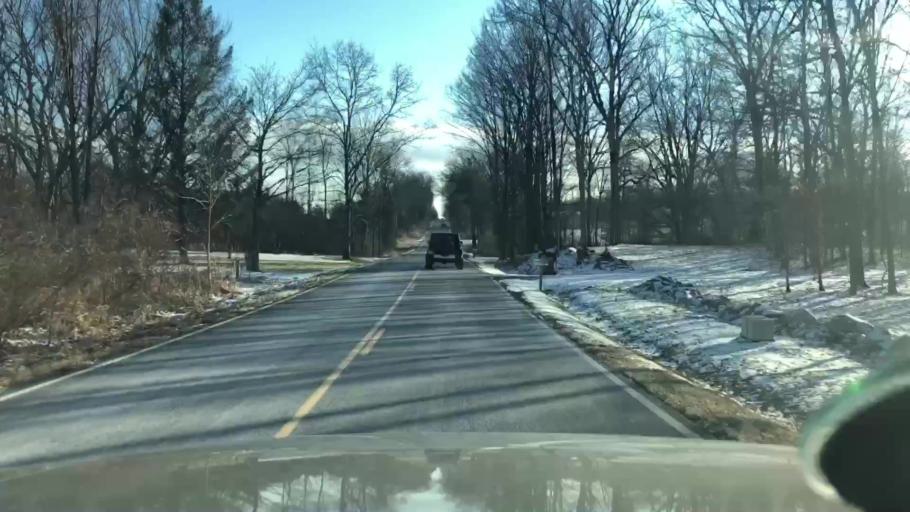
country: US
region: Michigan
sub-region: Jackson County
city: Vandercook Lake
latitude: 42.1320
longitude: -84.4516
